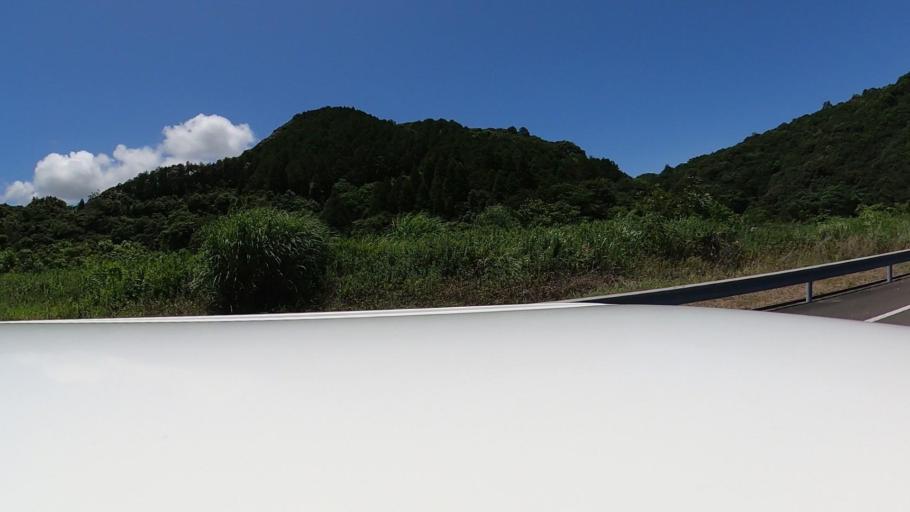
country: JP
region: Miyazaki
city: Nobeoka
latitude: 32.5306
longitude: 131.6647
